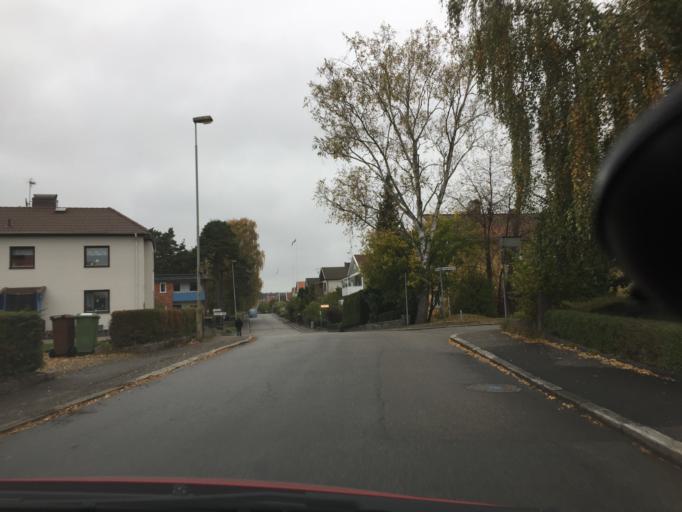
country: SE
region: Vaestra Goetaland
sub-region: Trollhattan
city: Trollhattan
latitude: 58.2819
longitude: 12.2988
